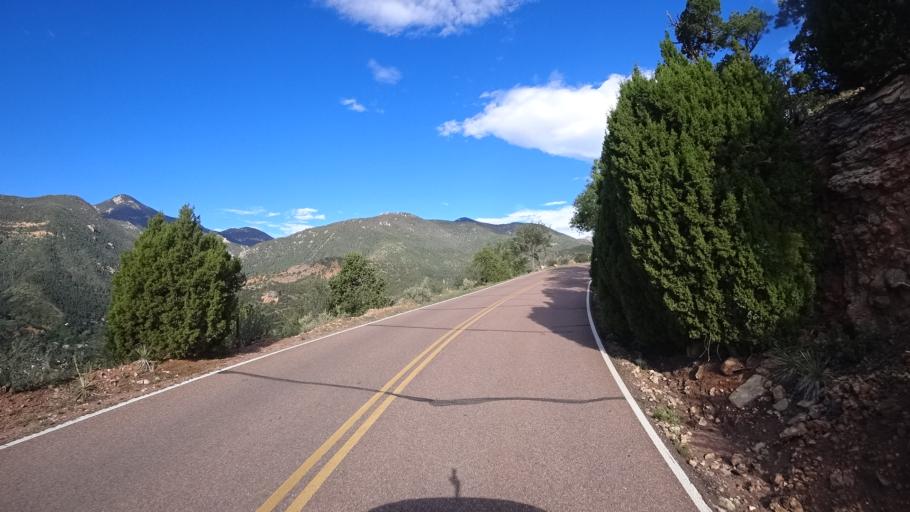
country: US
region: Colorado
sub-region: El Paso County
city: Manitou Springs
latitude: 38.8658
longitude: -104.9198
